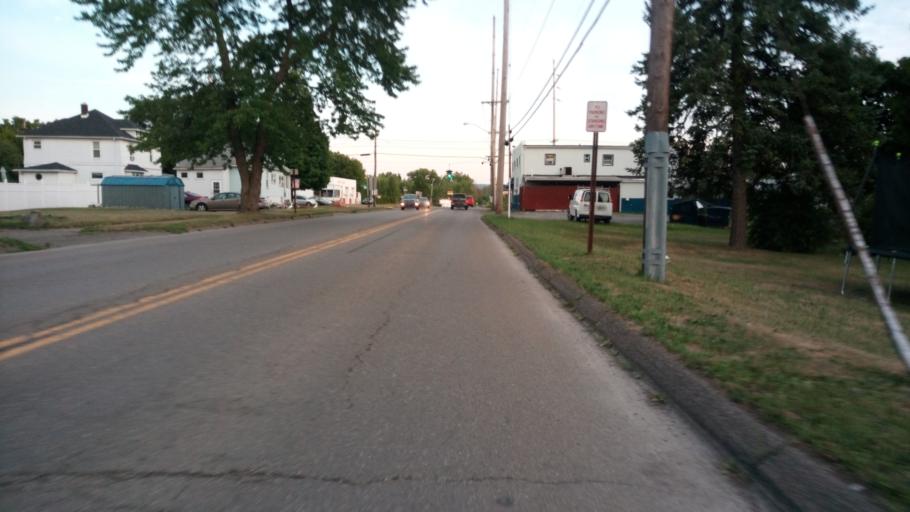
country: US
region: New York
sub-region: Chemung County
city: Elmira Heights
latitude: 42.1227
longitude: -76.8163
